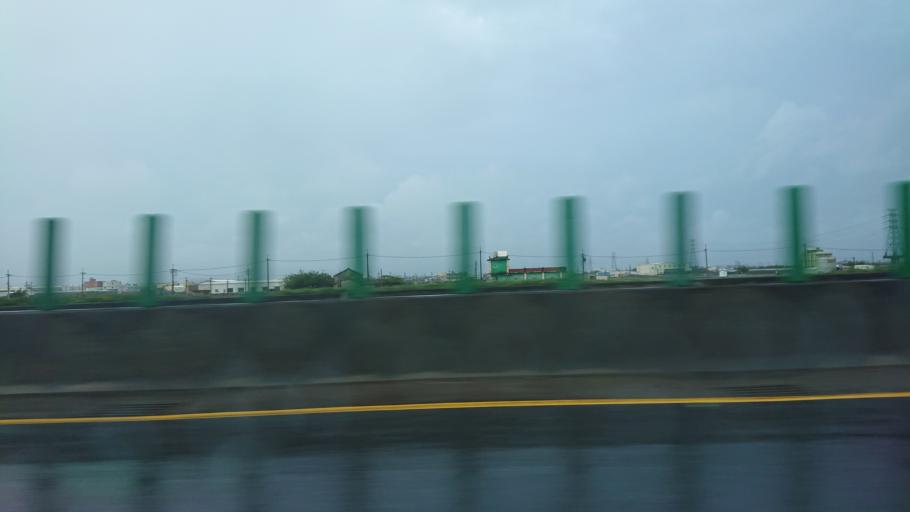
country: TW
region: Taiwan
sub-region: Changhua
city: Chang-hua
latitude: 24.1292
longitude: 120.4393
